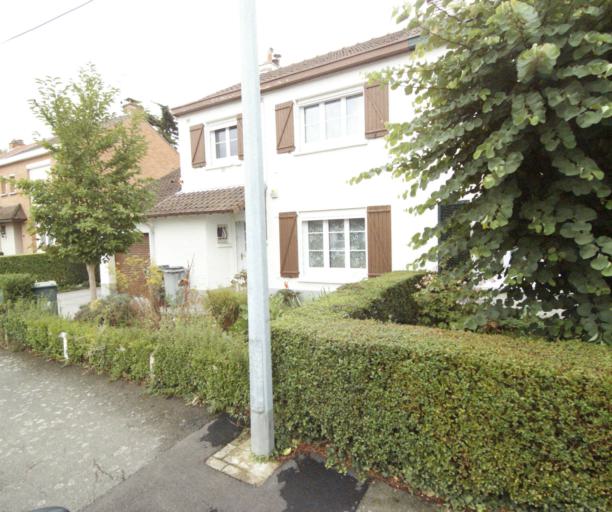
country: FR
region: Nord-Pas-de-Calais
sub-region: Departement du Nord
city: Ronchin
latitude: 50.5914
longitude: 3.0835
